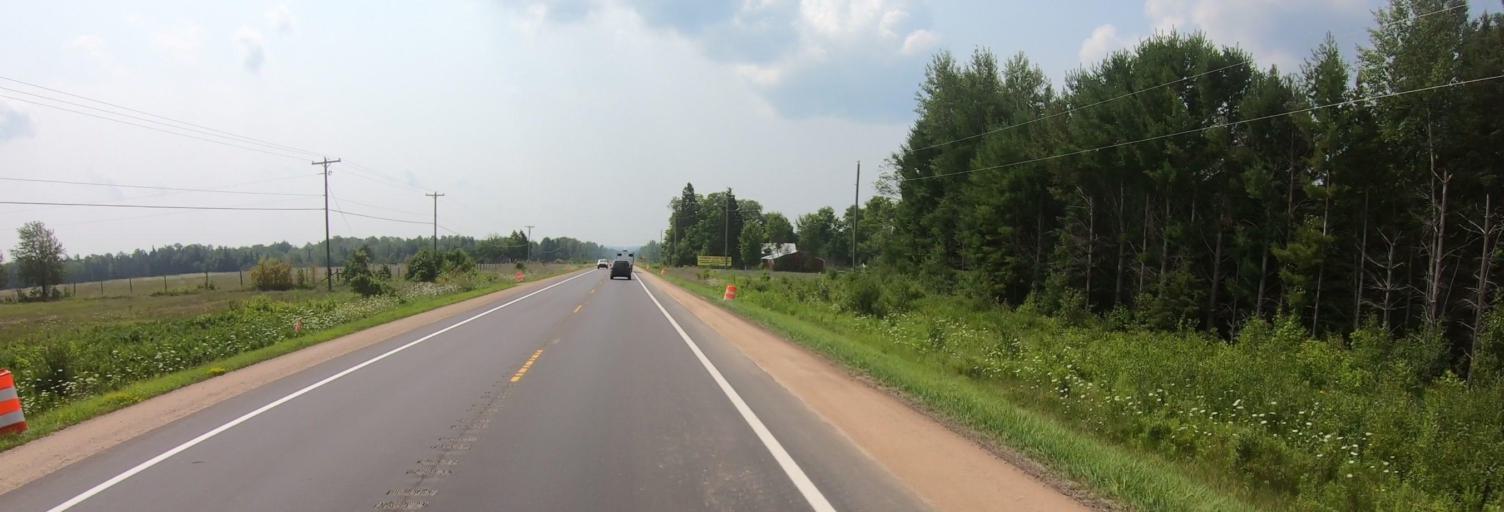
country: US
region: Michigan
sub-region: Luce County
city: Newberry
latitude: 46.4012
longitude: -85.5100
